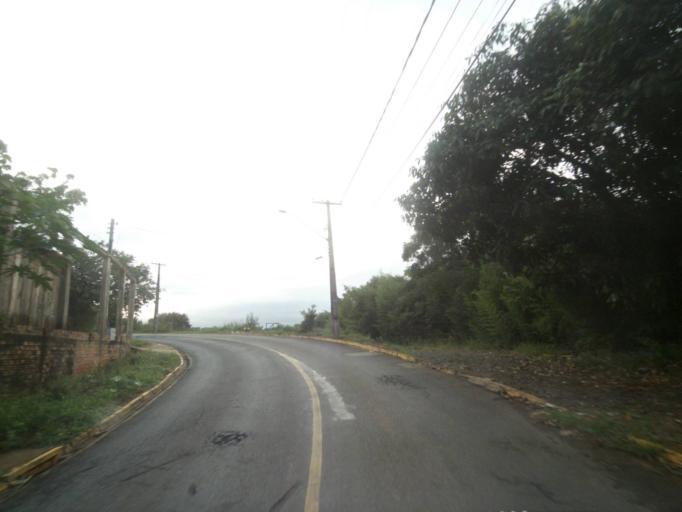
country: BR
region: Parana
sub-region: Telemaco Borba
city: Telemaco Borba
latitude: -24.3132
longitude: -50.6185
